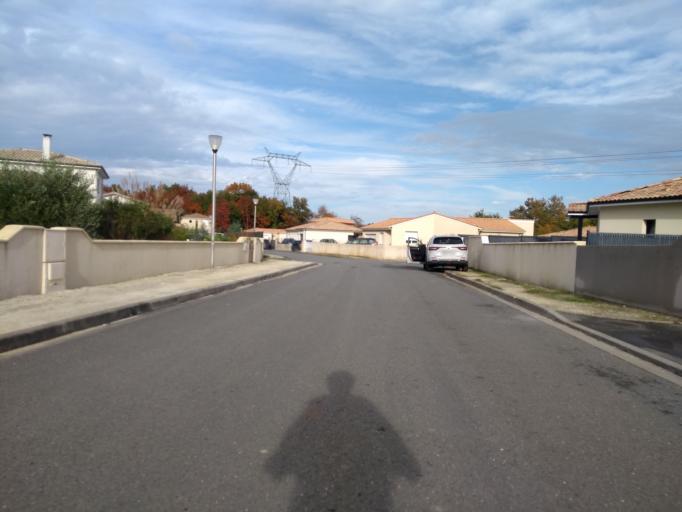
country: FR
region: Aquitaine
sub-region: Departement de la Gironde
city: Cestas
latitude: 44.7387
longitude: -0.6720
